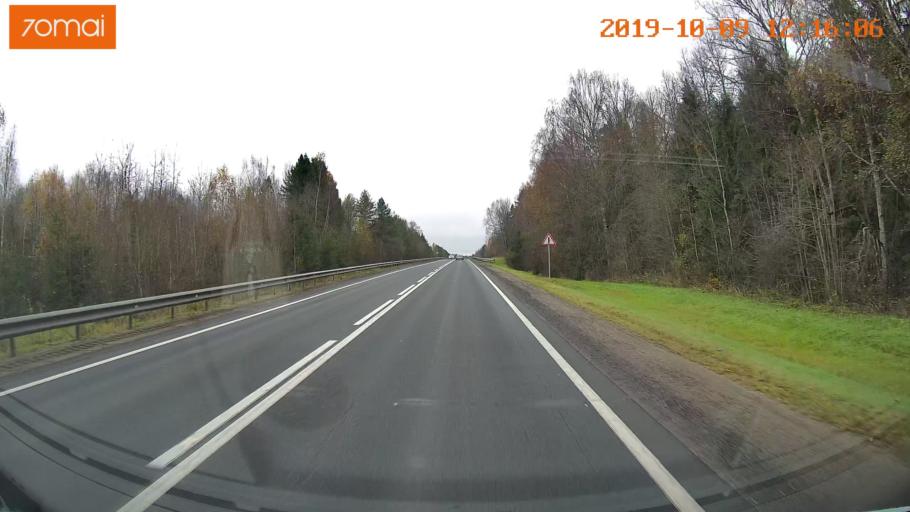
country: RU
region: Jaroslavl
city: Prechistoye
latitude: 58.4735
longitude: 40.3216
